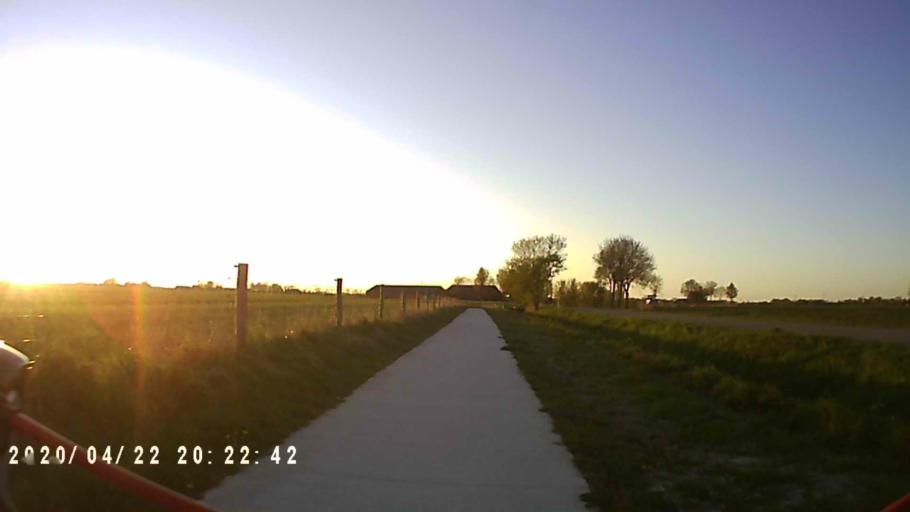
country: NL
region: Groningen
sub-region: Gemeente Winsum
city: Winsum
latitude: 53.3169
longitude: 6.5011
